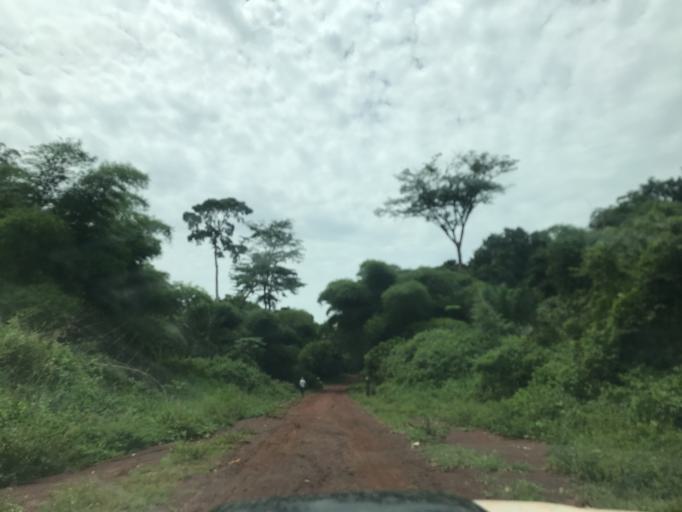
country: CD
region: Eastern Province
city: Buta
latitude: 2.3706
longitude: 24.9350
